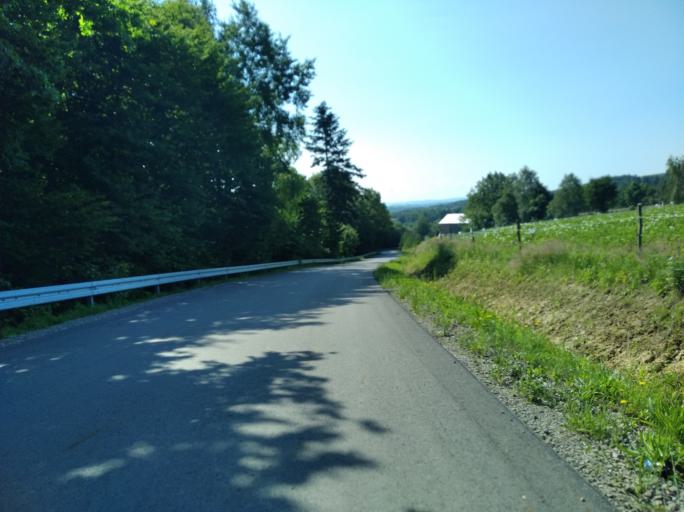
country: PL
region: Subcarpathian Voivodeship
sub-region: Powiat brzozowski
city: Wesola
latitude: 49.8341
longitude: 22.1443
